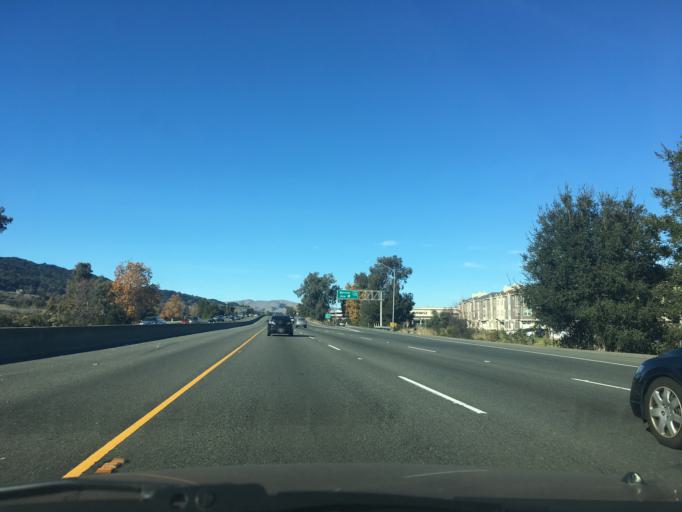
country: US
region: California
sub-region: Alameda County
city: Pleasanton
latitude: 37.6533
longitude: -121.8978
